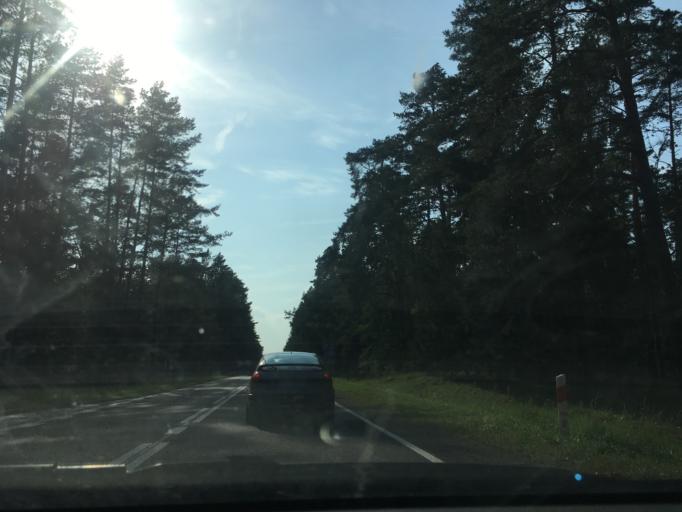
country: PL
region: Podlasie
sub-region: Powiat bialostocki
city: Suprasl
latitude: 53.1256
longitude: 23.3817
